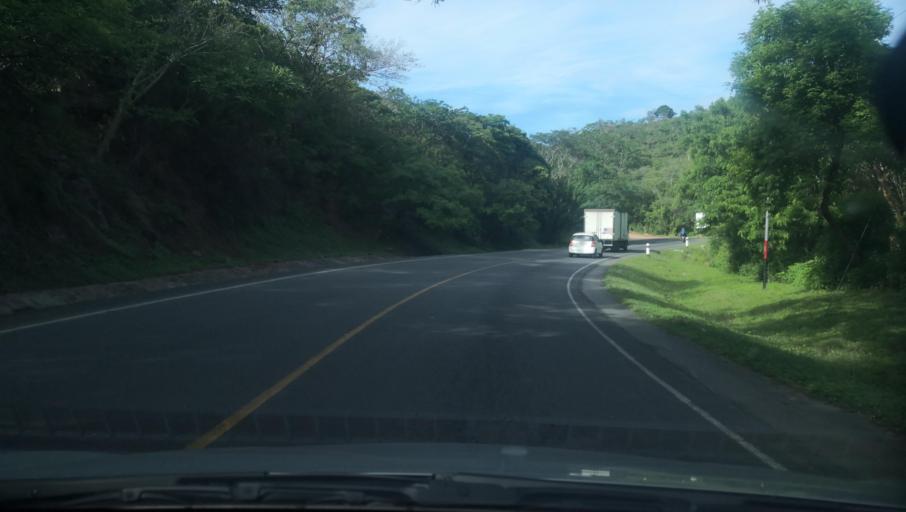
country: NI
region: Madriz
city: Totogalpa
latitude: 13.5861
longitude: -86.4755
